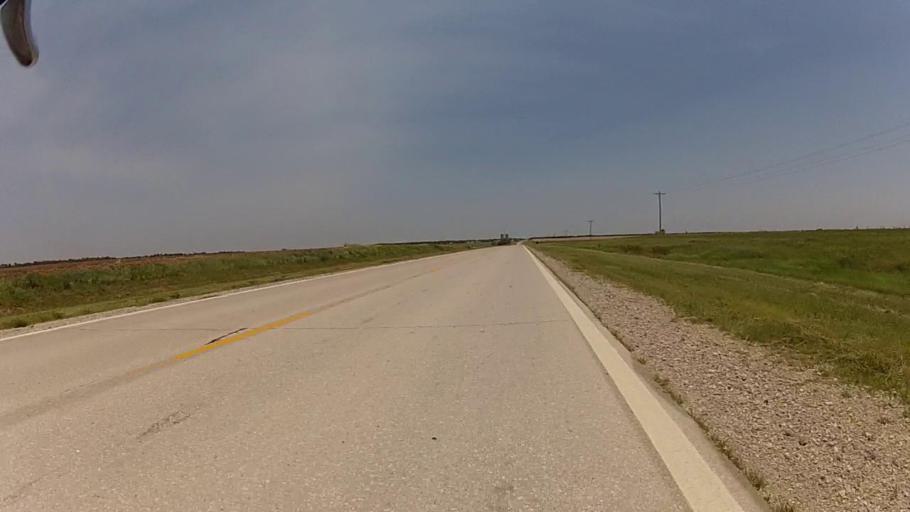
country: US
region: Kansas
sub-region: Cowley County
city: Arkansas City
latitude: 37.0574
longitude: -97.2627
